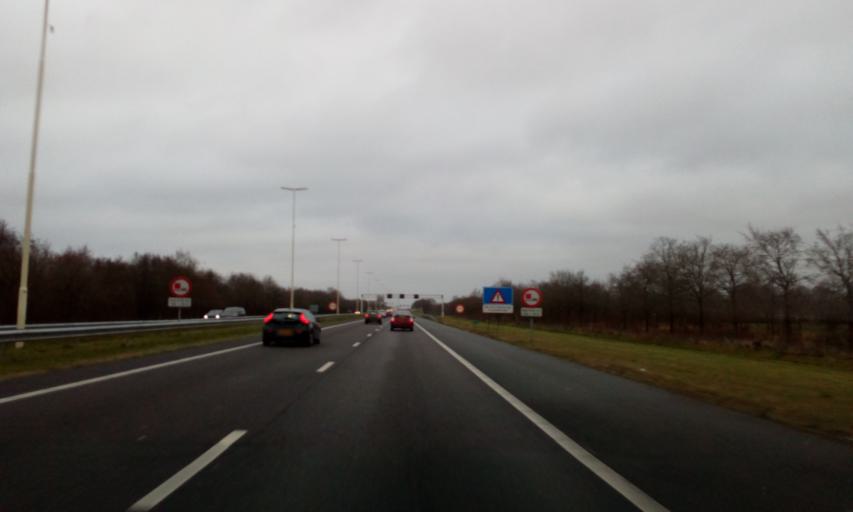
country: NL
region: Utrecht
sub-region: Gemeente De Bilt
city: De Bilt
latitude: 52.1496
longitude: 5.1630
